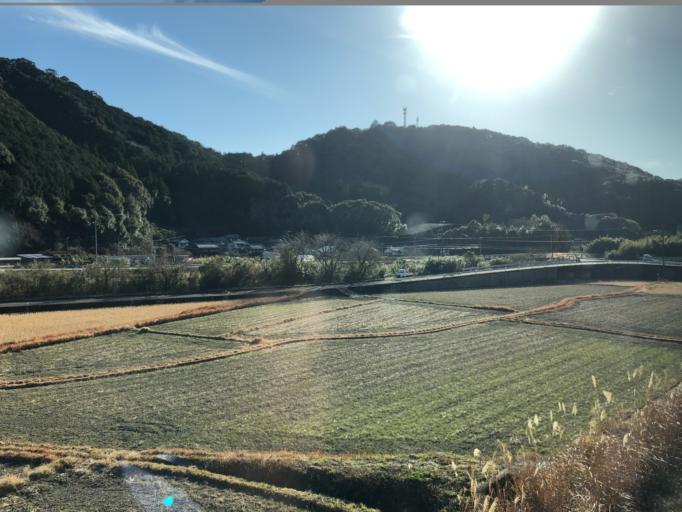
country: JP
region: Kochi
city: Nakamura
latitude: 33.1113
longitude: 133.1095
